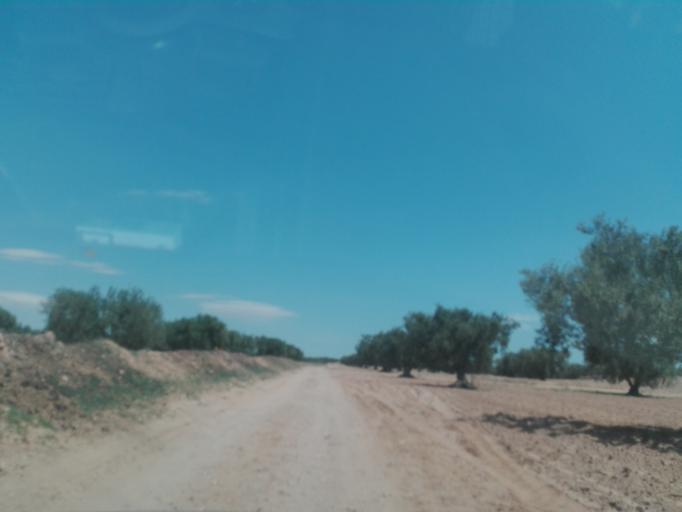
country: TN
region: Safaqis
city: Sfax
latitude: 34.6593
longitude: 10.6008
